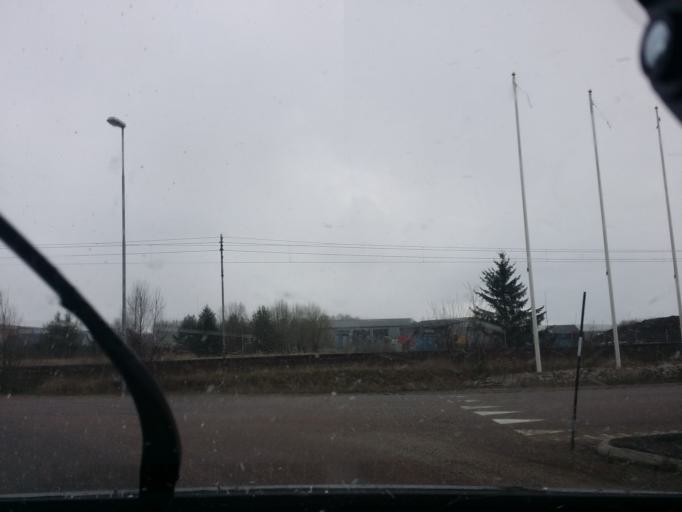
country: SE
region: Vaestmanland
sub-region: Sala Kommun
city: Sala
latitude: 59.9102
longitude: 16.6192
